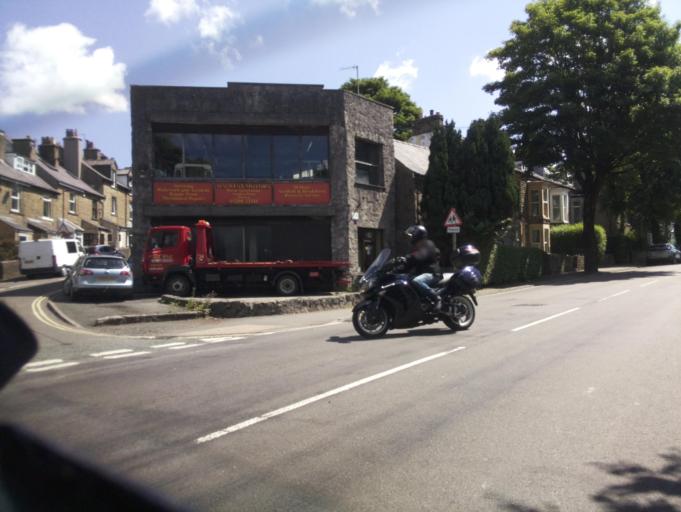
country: GB
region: England
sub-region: Derbyshire
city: Buxton
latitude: 53.2526
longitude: -1.9134
